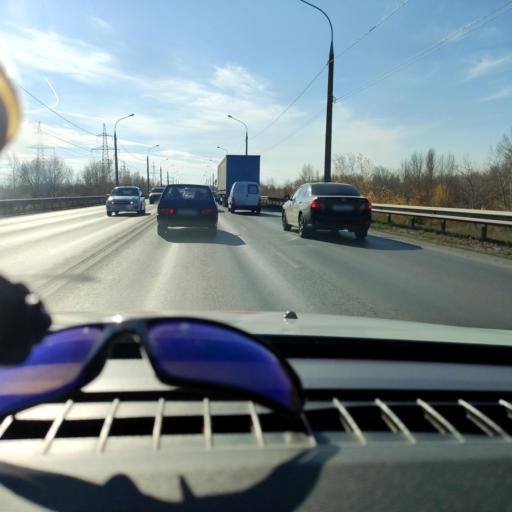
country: RU
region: Samara
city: Samara
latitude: 53.1626
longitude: 50.1942
